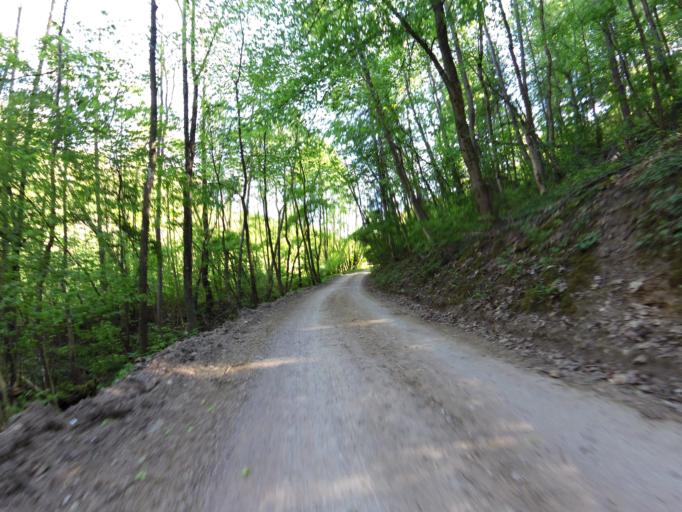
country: LT
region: Vilnius County
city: Pilaite
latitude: 54.6861
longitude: 25.1560
